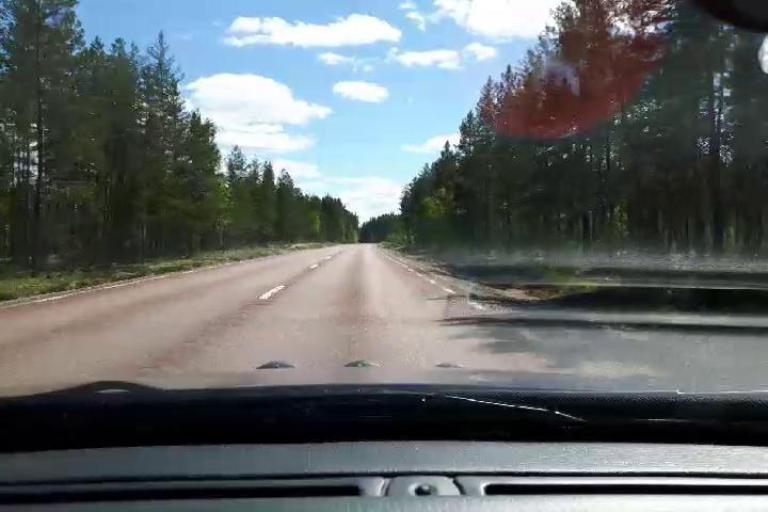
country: SE
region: Gaevleborg
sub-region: Ljusdals Kommun
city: Farila
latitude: 61.8252
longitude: 15.7552
